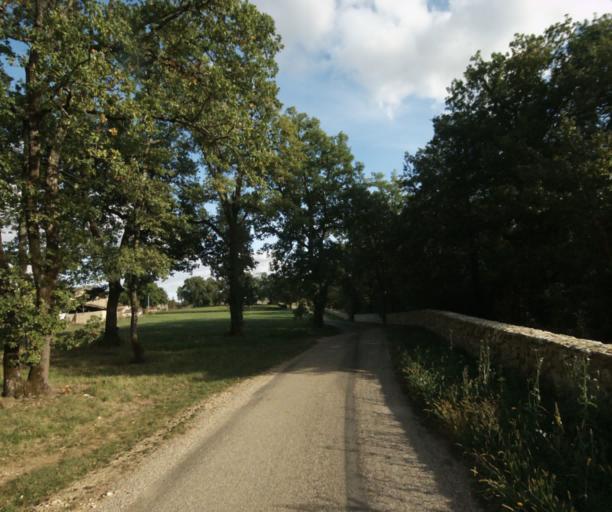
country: FR
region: Midi-Pyrenees
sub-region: Departement du Gers
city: Gondrin
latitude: 43.8945
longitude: 0.2703
